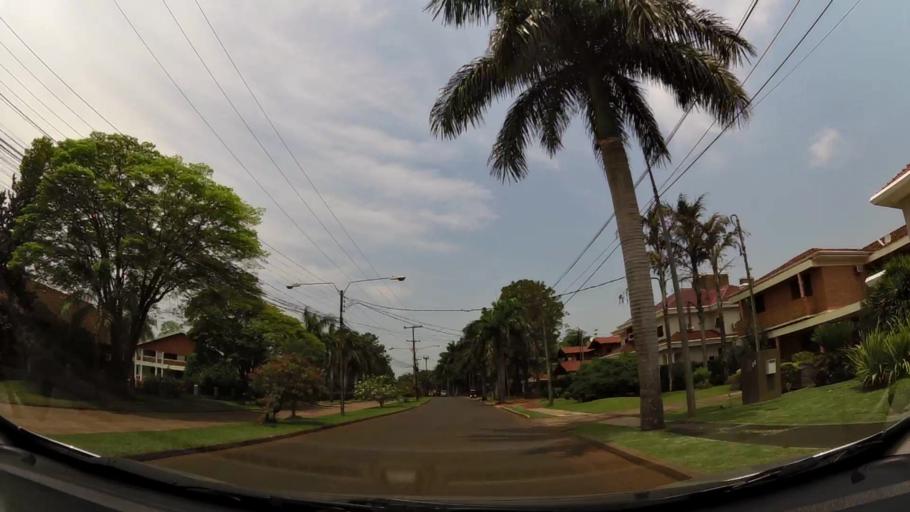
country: PY
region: Alto Parana
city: Ciudad del Este
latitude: -25.4873
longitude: -54.6165
